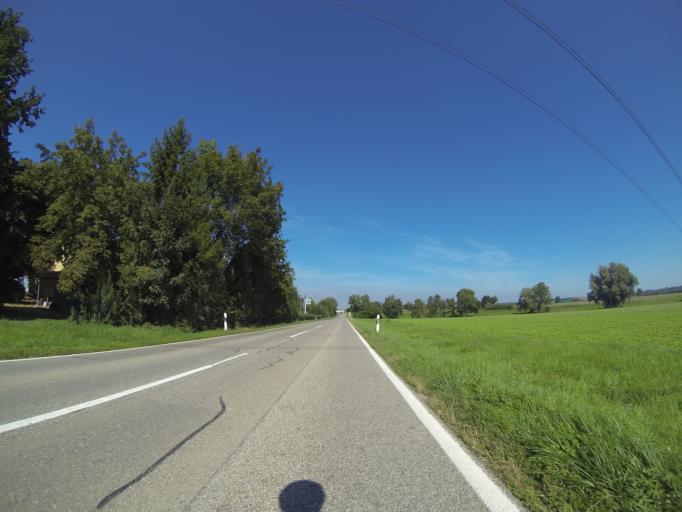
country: DE
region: Baden-Wuerttemberg
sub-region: Tuebingen Region
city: Achstetten
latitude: 48.2955
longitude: 9.9068
